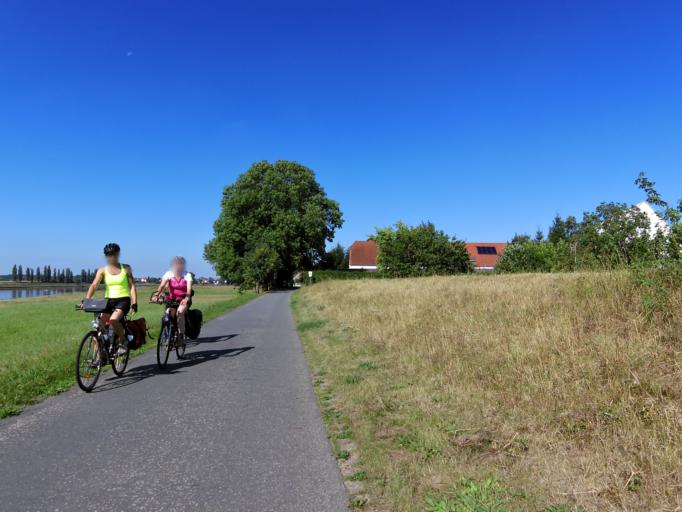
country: DE
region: Saxony
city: Strehla
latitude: 51.3491
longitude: 13.2684
